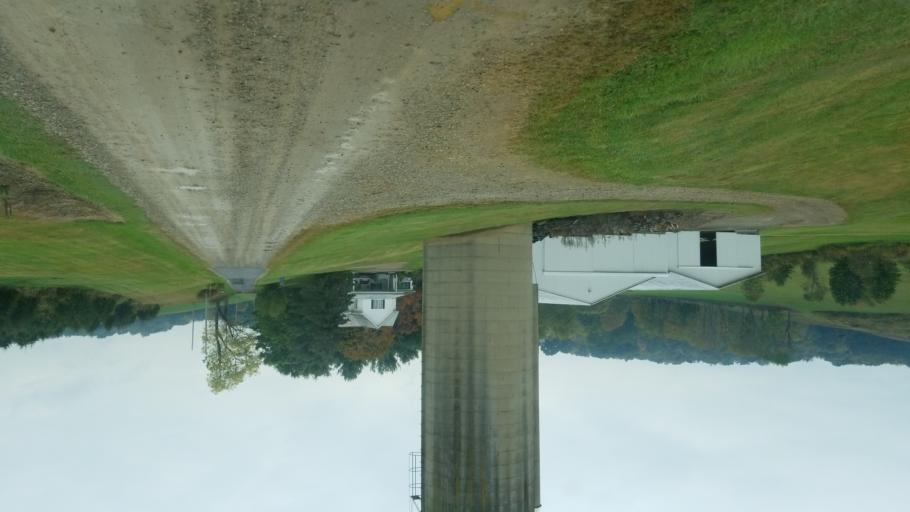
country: US
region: Ohio
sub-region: Knox County
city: Danville
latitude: 40.5145
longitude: -82.3314
